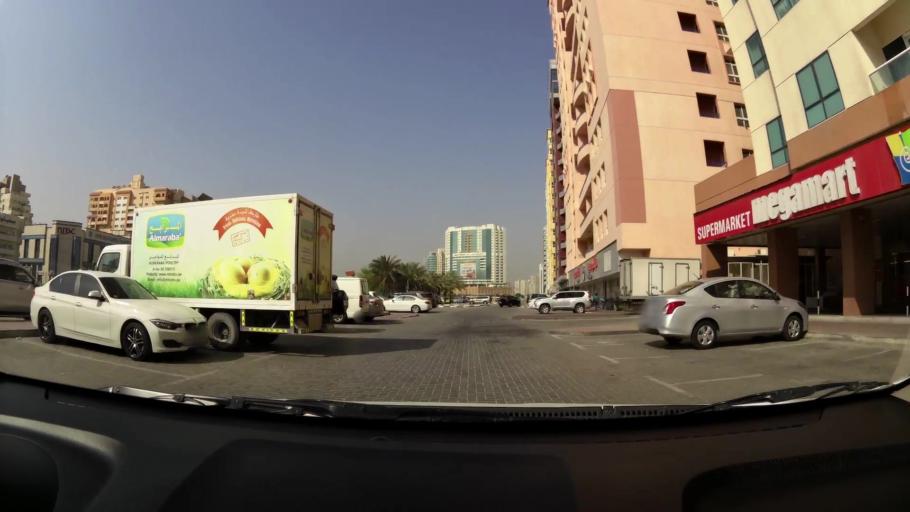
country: AE
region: Ash Shariqah
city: Sharjah
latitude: 25.2917
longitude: 55.3689
